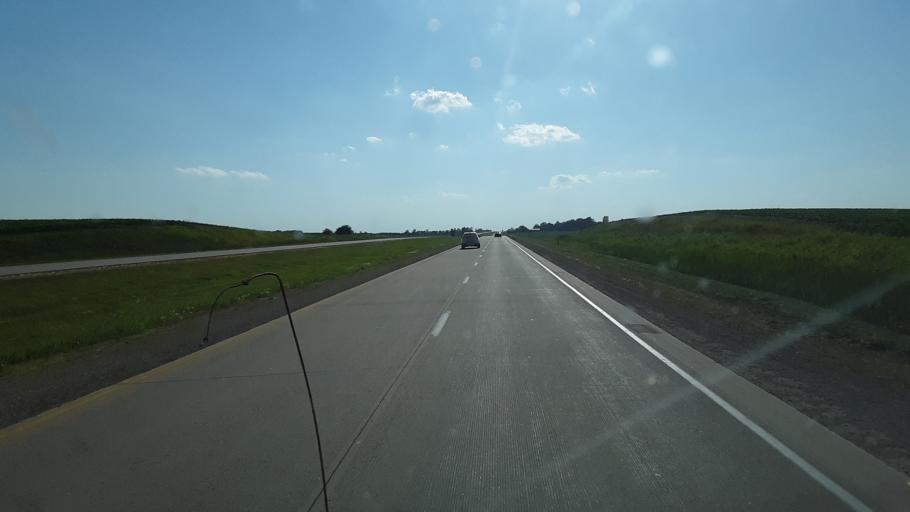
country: US
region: Iowa
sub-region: Grundy County
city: Dike
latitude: 42.4635
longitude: -92.7146
